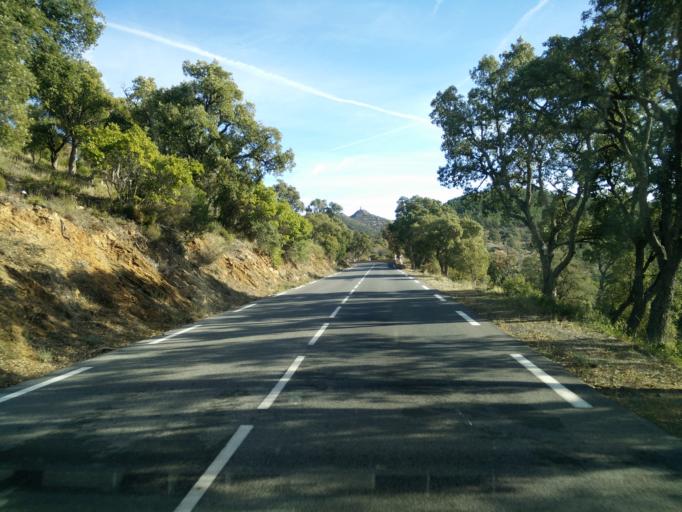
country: FR
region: Provence-Alpes-Cote d'Azur
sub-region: Departement du Var
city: Saint-Raphael
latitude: 43.5012
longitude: 6.7911
